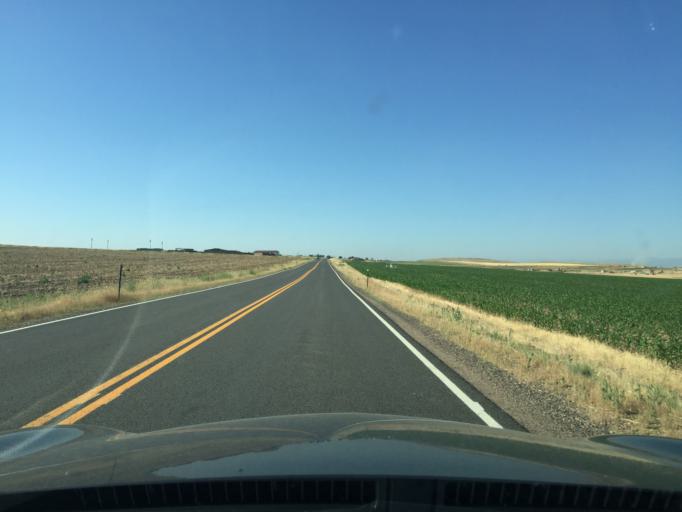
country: US
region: Colorado
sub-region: Boulder County
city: Erie
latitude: 40.0552
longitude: -105.0182
